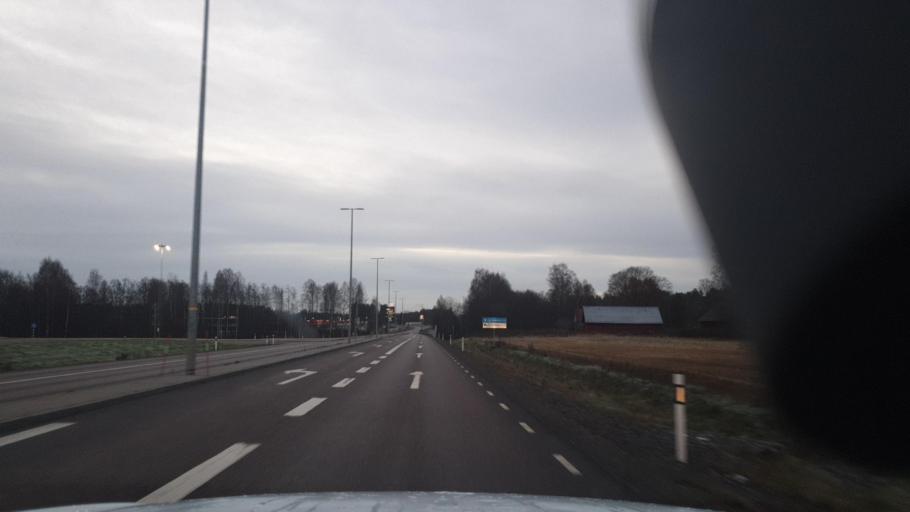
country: SE
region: Vaermland
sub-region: Eda Kommun
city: Charlottenberg
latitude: 59.8851
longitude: 12.2820
